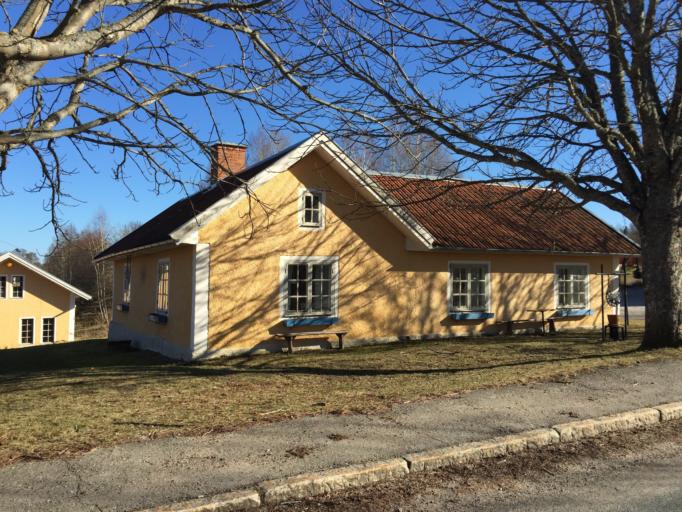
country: SE
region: OErebro
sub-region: Orebro Kommun
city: Odensbacken
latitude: 59.0115
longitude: 15.5824
